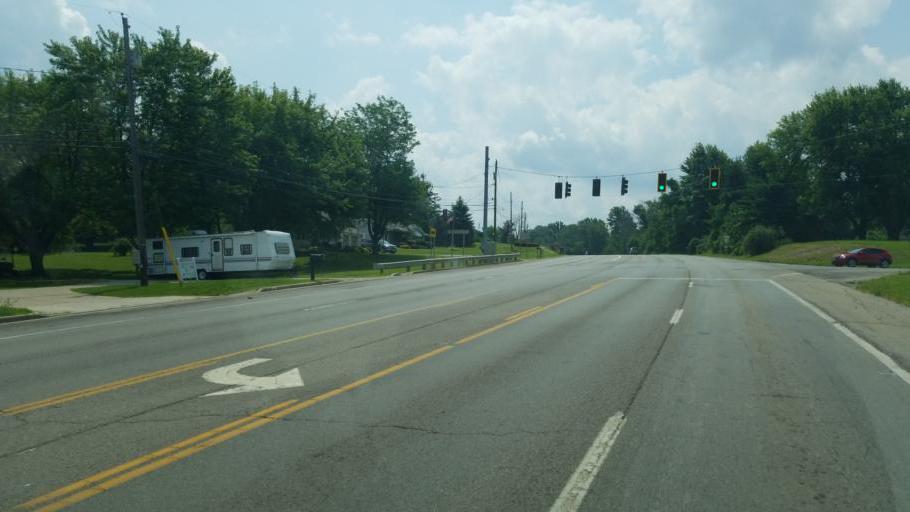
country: US
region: Ohio
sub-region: Richland County
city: Ontario
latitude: 40.8092
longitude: -82.5900
